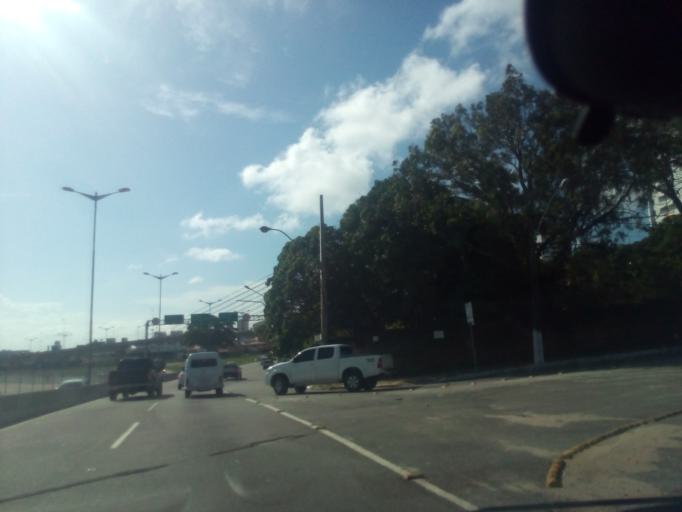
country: BR
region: Rio Grande do Norte
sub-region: Natal
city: Natal
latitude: -5.8248
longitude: -35.2129
